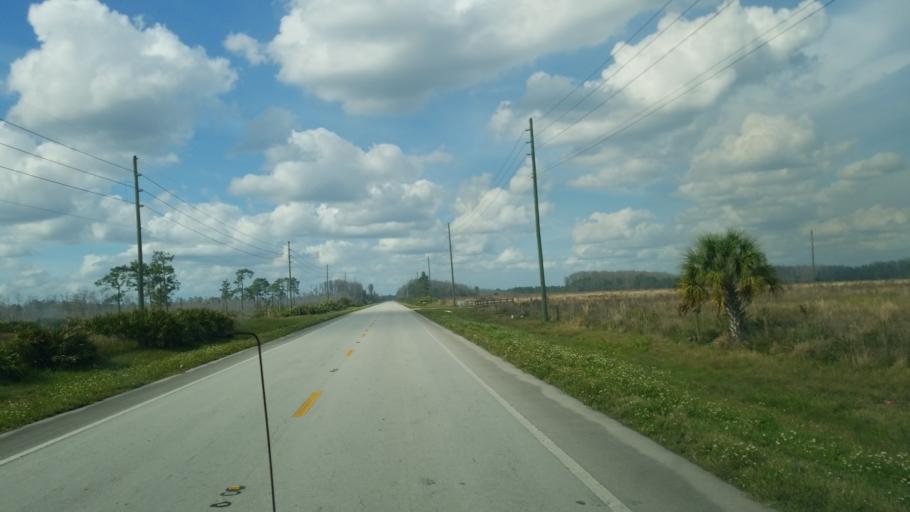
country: US
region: Florida
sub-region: Osceola County
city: Saint Cloud
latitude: 28.0589
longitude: -81.0590
